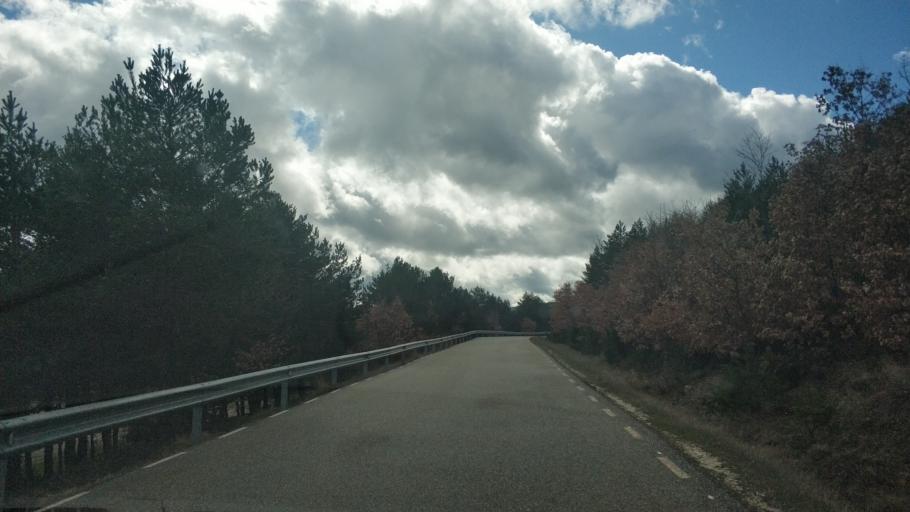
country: ES
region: Castille and Leon
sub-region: Provincia de Burgos
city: Quintanar de la Sierra
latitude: 41.9938
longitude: -3.0242
